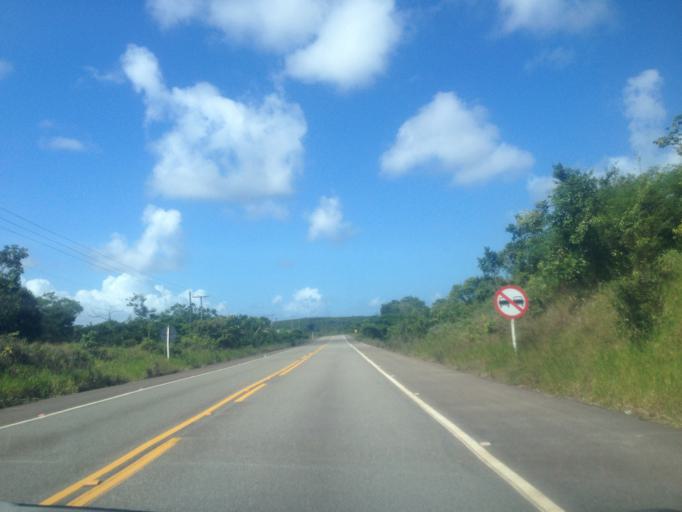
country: BR
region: Sergipe
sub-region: Indiaroba
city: Indiaroba
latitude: -11.4868
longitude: -37.4796
